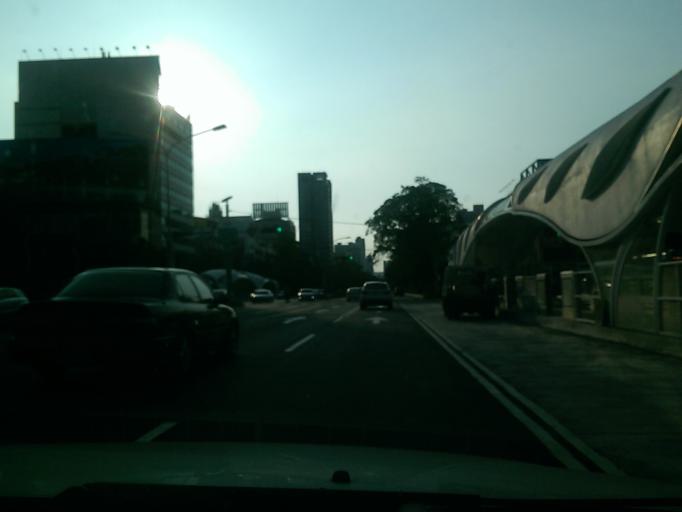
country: TW
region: Taiwan
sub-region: Taichung City
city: Taichung
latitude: 24.1589
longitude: 120.6566
